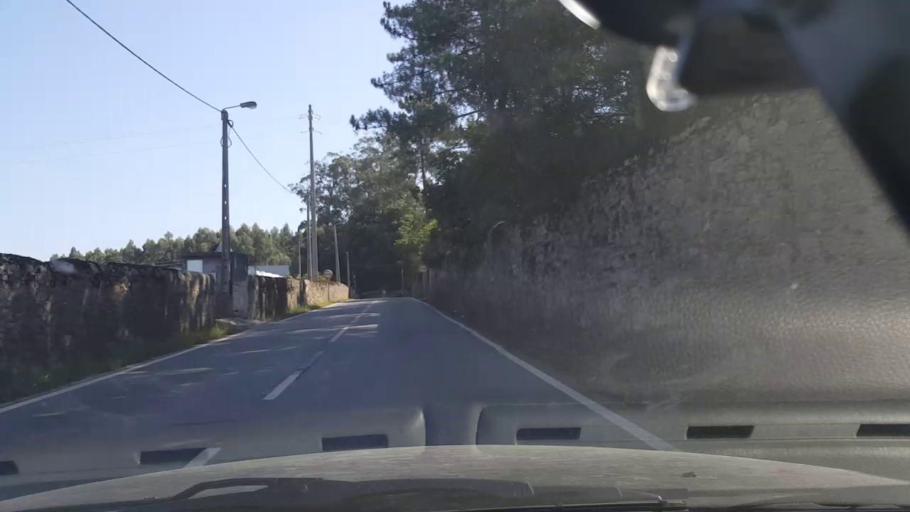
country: PT
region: Porto
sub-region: Vila do Conde
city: Arvore
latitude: 41.3645
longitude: -8.6714
